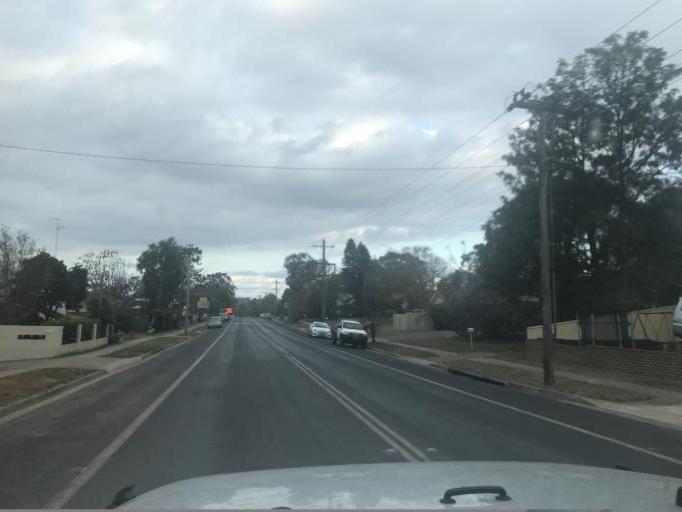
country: AU
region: New South Wales
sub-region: Hawkesbury
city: Richmond
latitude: -33.5833
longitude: 150.7148
